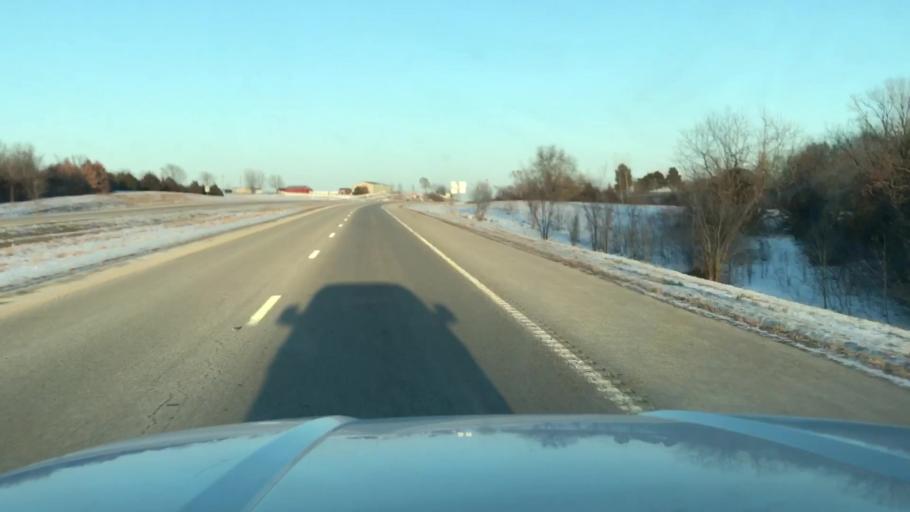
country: US
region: Missouri
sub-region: Clinton County
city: Gower
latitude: 39.7597
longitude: -94.5718
